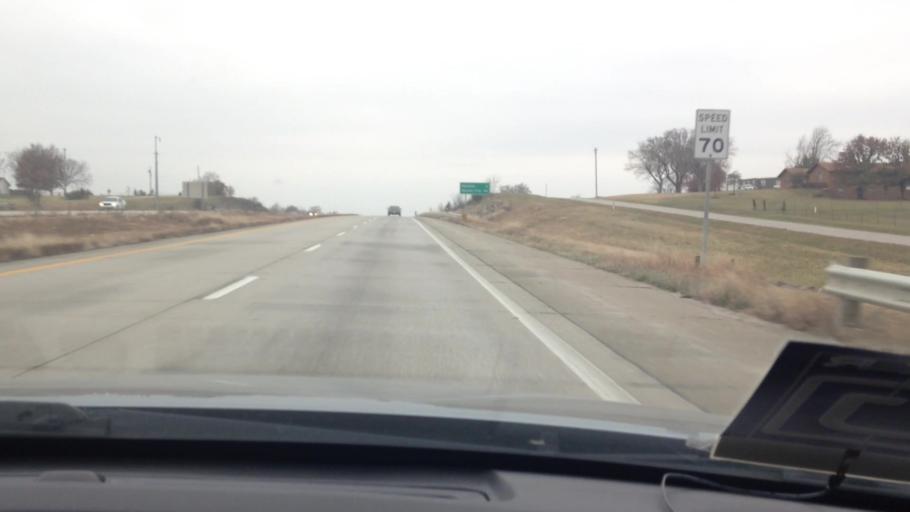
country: US
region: Missouri
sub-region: Cass County
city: Harrisonville
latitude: 38.6632
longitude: -94.3809
